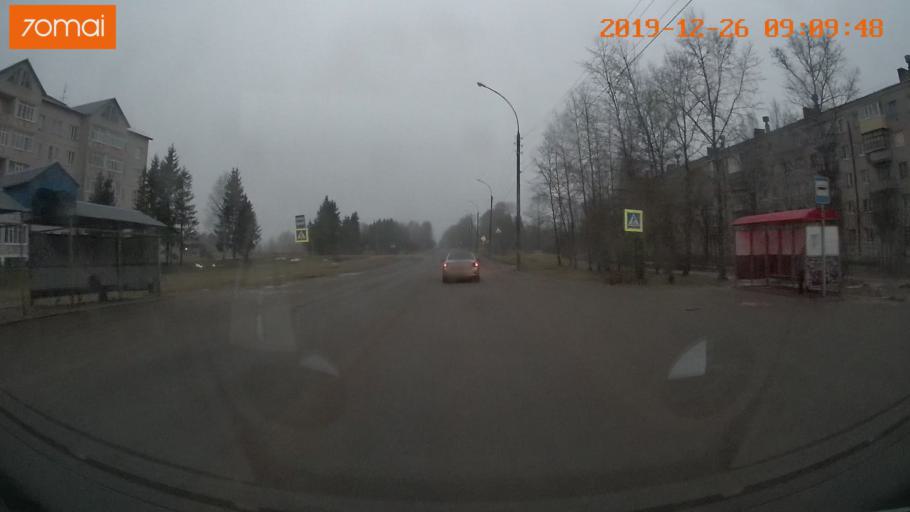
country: RU
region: Vologda
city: Gryazovets
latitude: 58.8667
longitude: 40.2527
